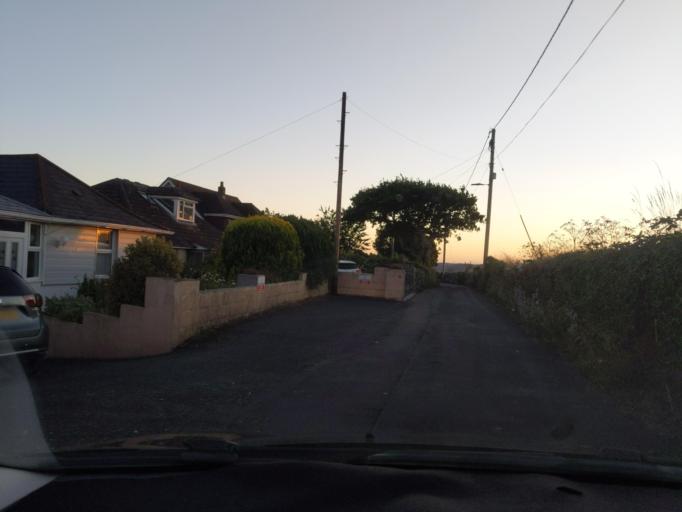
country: GB
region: England
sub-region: Plymouth
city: Plymstock
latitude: 50.3558
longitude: -4.0919
